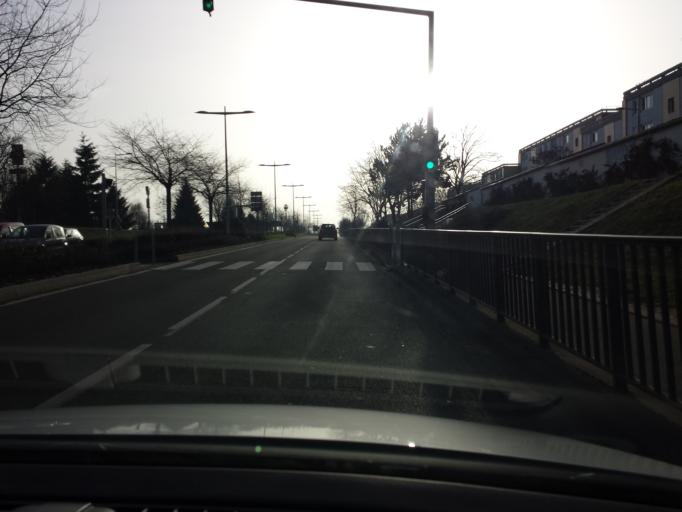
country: FR
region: Haute-Normandie
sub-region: Departement de l'Eure
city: Evreux
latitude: 49.0151
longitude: 1.1700
